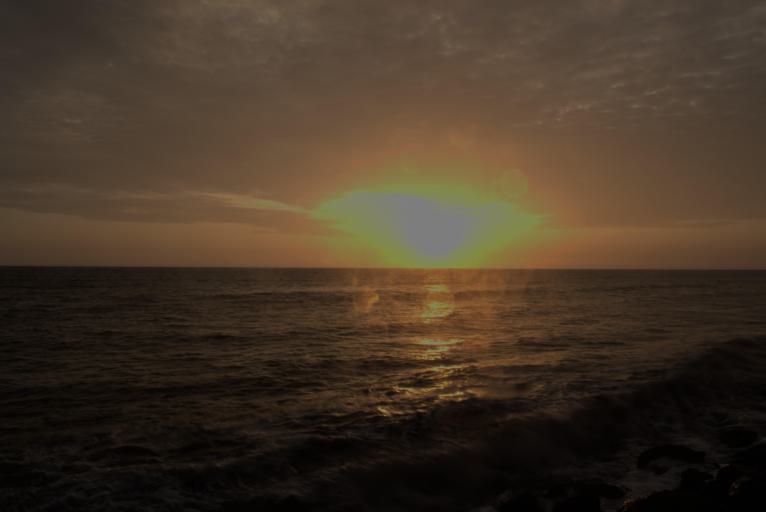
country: PE
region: La Libertad
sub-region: Provincia de Trujillo
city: Buenos Aires
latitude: -8.1396
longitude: -79.0622
